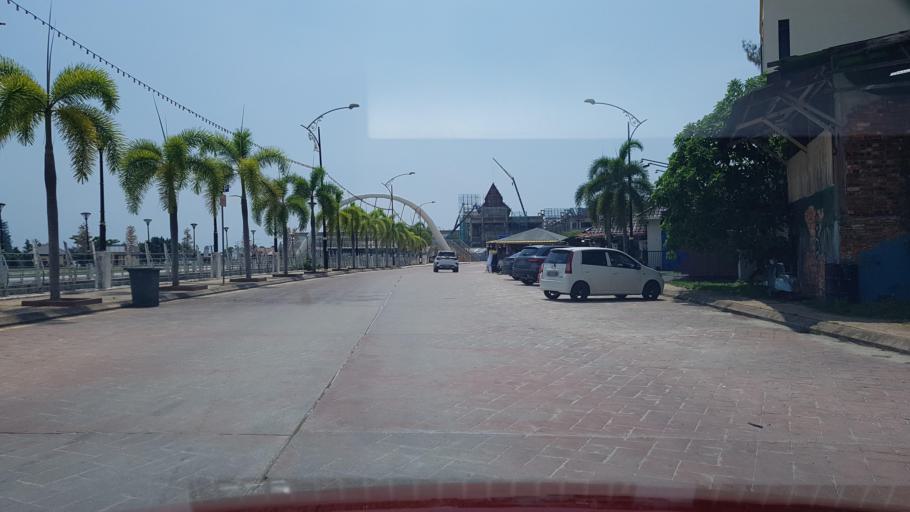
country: MY
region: Terengganu
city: Kuala Terengganu
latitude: 5.3349
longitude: 103.1335
